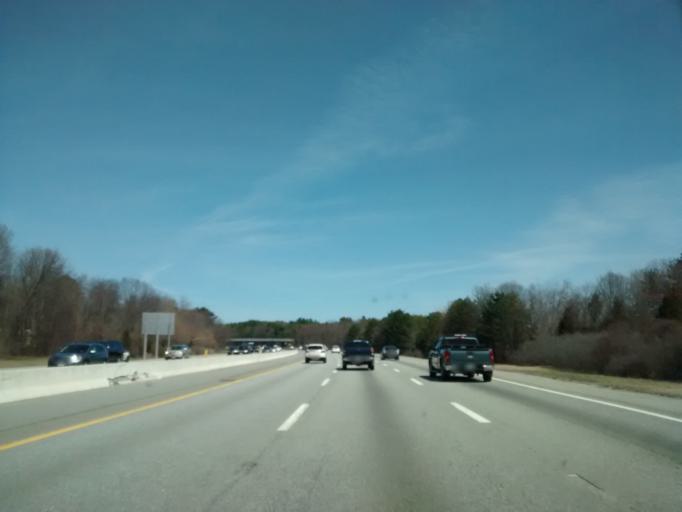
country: US
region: Massachusetts
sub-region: Middlesex County
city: Cochituate
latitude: 42.3179
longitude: -71.3477
